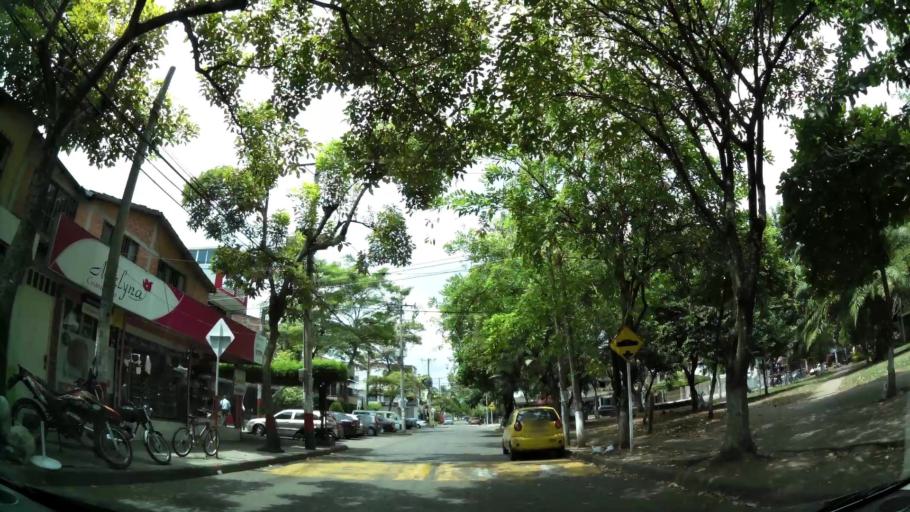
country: CO
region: Valle del Cauca
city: Cali
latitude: 3.4755
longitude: -76.4961
